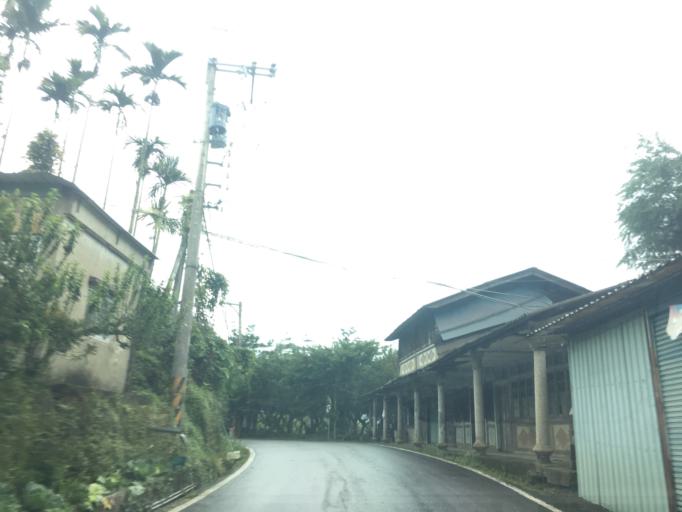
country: TW
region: Taiwan
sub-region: Yunlin
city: Douliu
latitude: 23.5576
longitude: 120.6675
